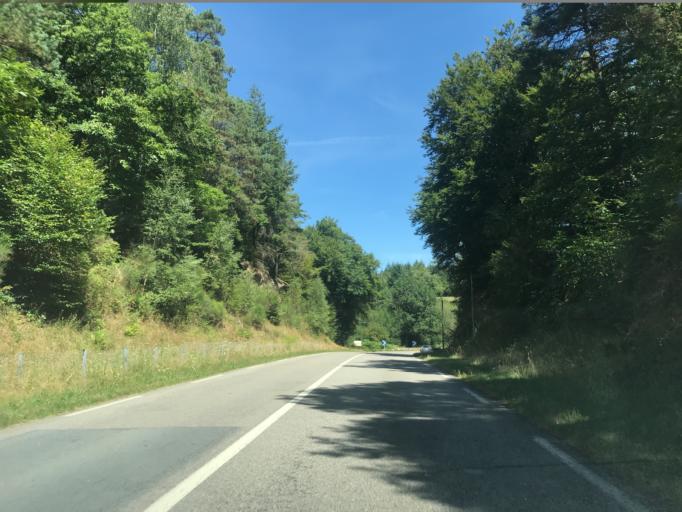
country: FR
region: Limousin
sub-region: Departement de la Correze
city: Egletons
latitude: 45.3549
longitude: 1.9699
